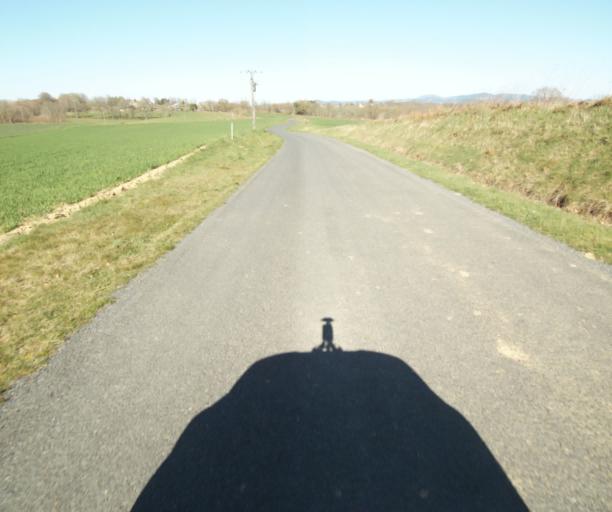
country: FR
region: Limousin
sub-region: Departement de la Correze
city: Chamboulive
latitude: 45.4344
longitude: 1.6695
